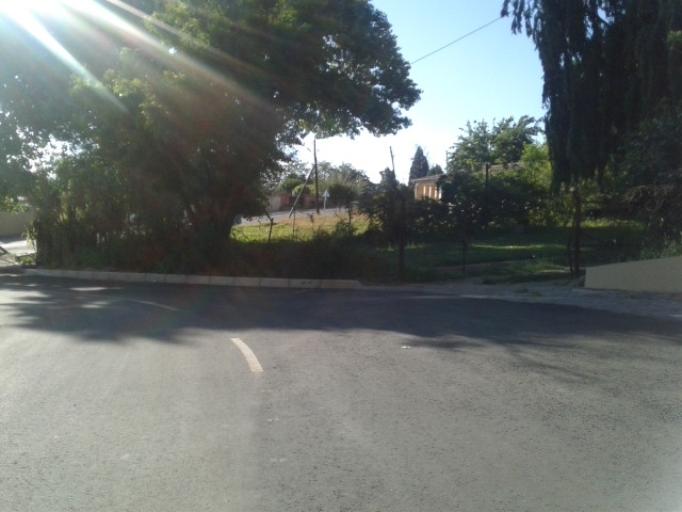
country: LS
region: Maseru
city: Maseru
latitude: -29.3071
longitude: 27.4728
